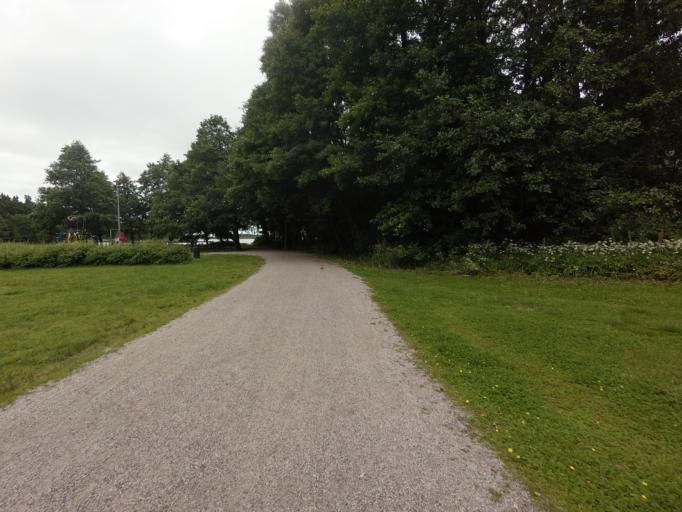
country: FI
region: Uusimaa
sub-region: Helsinki
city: Otaniemi
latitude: 60.1769
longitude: 24.8214
